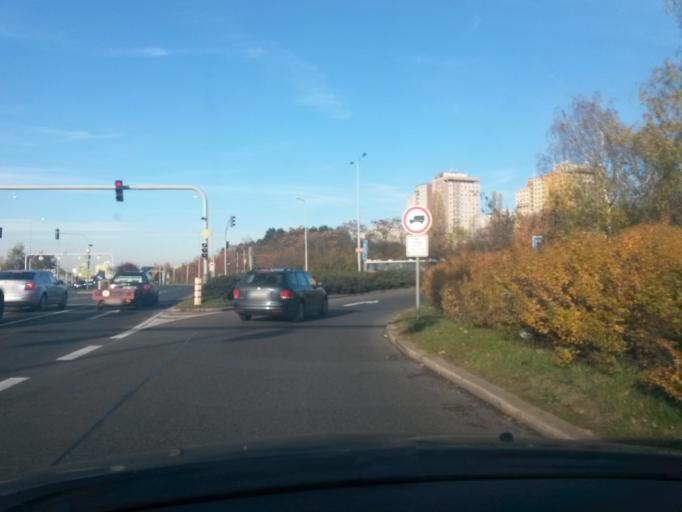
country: CZ
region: Central Bohemia
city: Vestec
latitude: 50.0234
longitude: 14.5090
